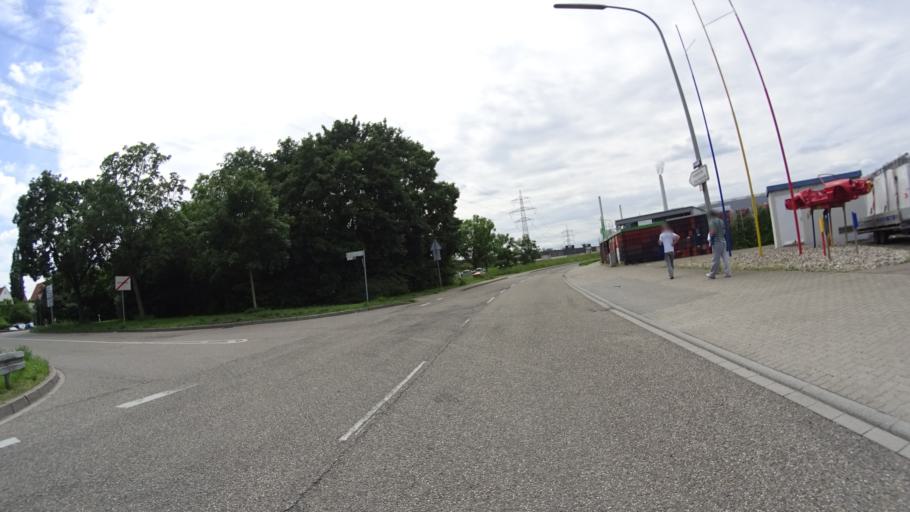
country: DE
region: Baden-Wuerttemberg
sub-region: Karlsruhe Region
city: Rheinstetten
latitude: 49.0081
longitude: 8.3262
